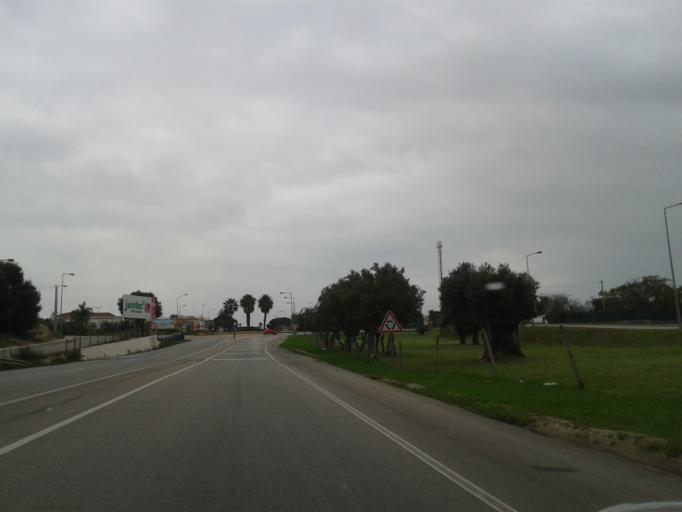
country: PT
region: Faro
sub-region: Lagoa
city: Lagoa
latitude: 37.1360
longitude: -8.4612
